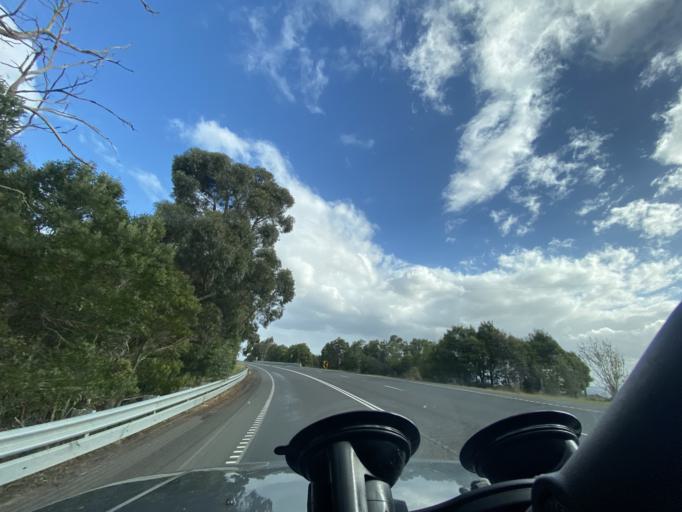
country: AU
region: Victoria
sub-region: Murrindindi
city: Kinglake West
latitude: -37.4865
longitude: 145.1834
